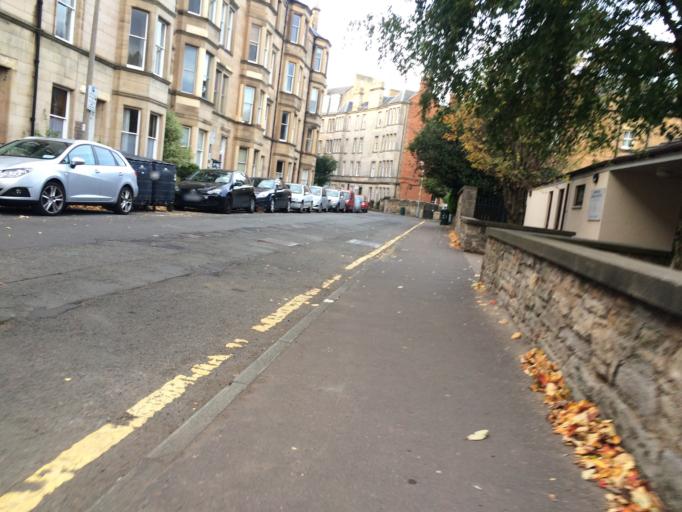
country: GB
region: Scotland
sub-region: Edinburgh
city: Edinburgh
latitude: 55.9357
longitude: -3.2074
